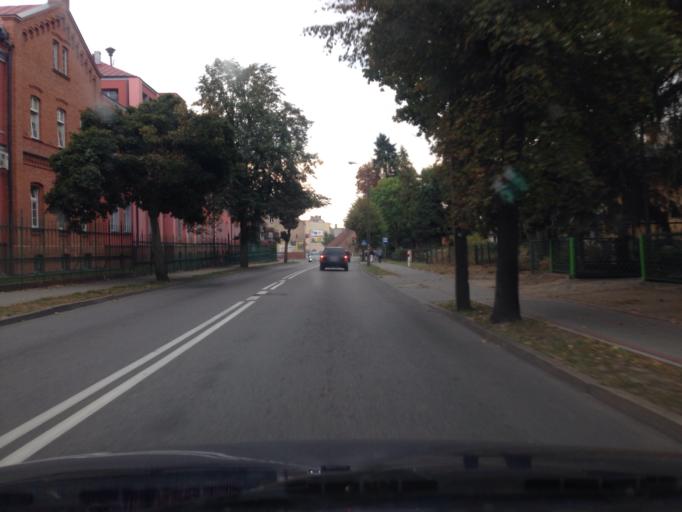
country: PL
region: Pomeranian Voivodeship
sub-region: Powiat malborski
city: Malbork
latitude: 54.0318
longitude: 19.0221
